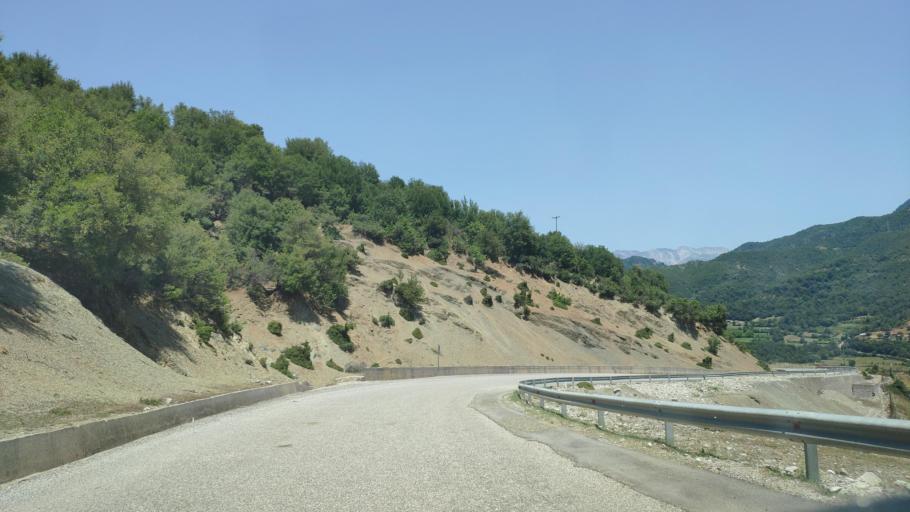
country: GR
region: Thessaly
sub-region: Nomos Kardhitsas
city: Anthiro
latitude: 39.1604
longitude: 21.3803
